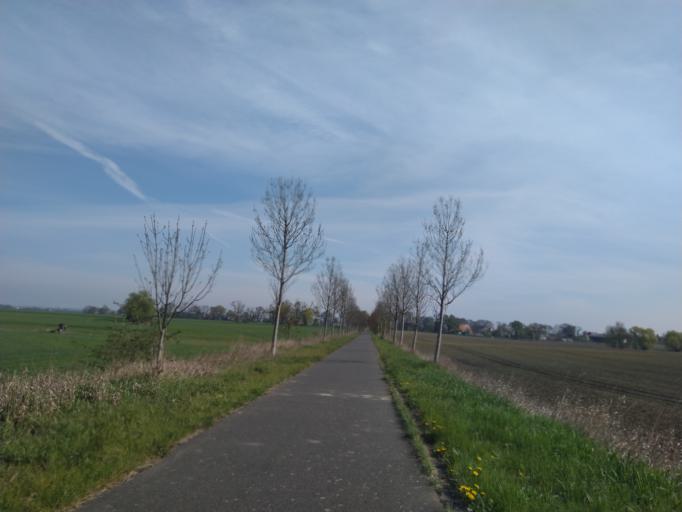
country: DE
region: Brandenburg
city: Wriezen
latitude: 52.7370
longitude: 14.1561
